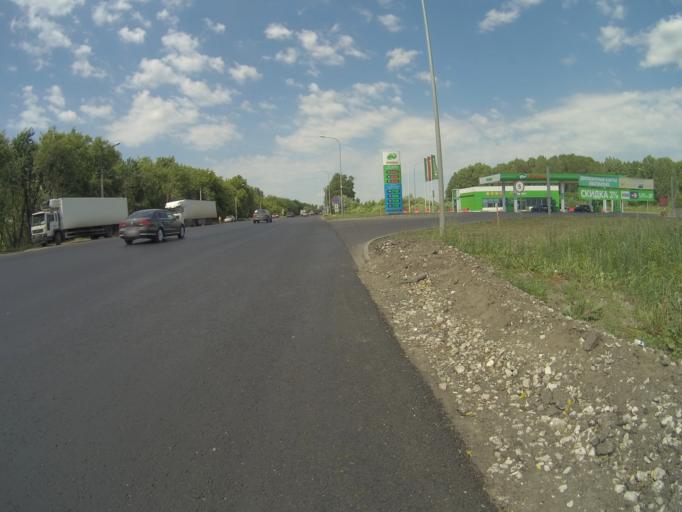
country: RU
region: Vladimir
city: Kommunar
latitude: 56.1780
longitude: 40.4544
